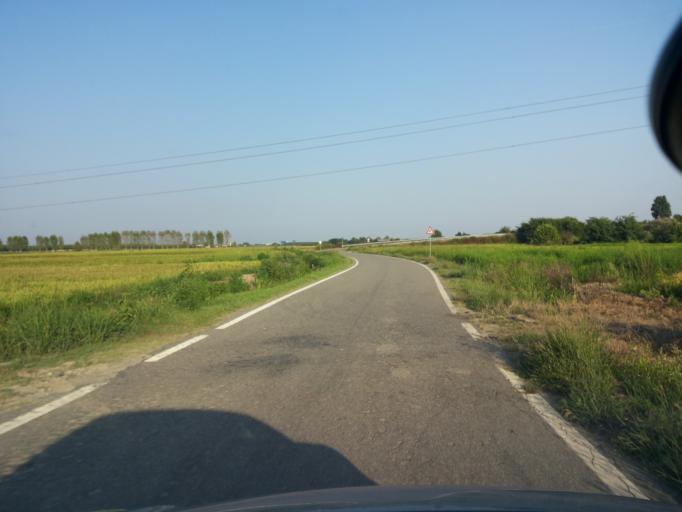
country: IT
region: Piedmont
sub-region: Provincia di Vercelli
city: Lignana
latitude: 45.3015
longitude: 8.3505
